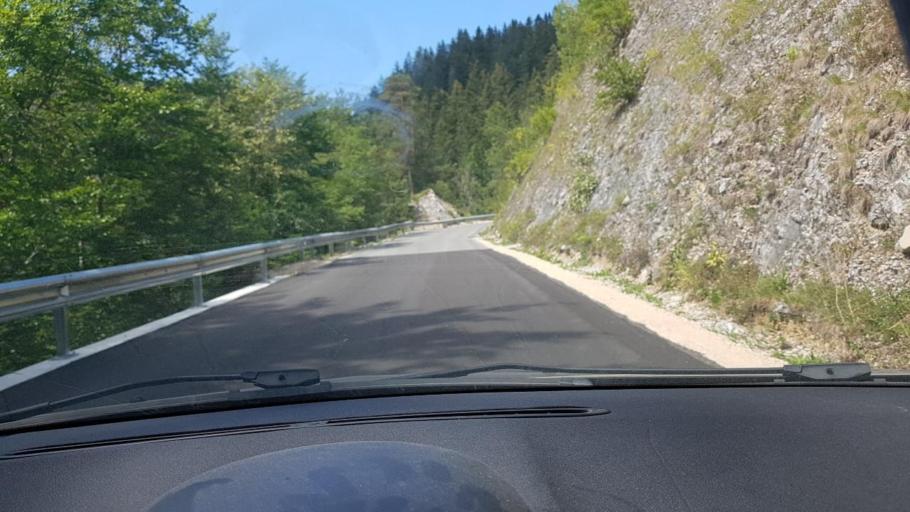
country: SI
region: Solcava
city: Solcava
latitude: 46.4192
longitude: 14.6255
